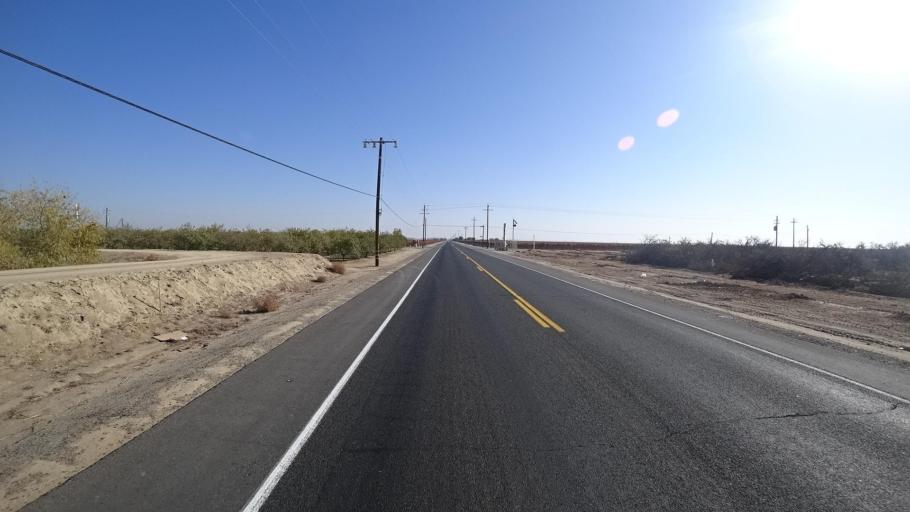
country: US
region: California
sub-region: Kern County
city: Delano
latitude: 35.7180
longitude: -119.2776
